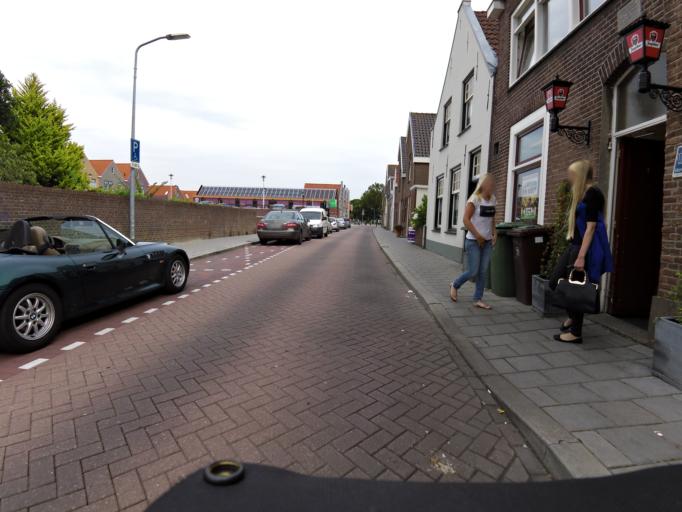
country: NL
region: South Holland
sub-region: Gemeente Goeree-Overflakkee
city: Middelharnis
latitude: 51.6897
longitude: 4.2117
